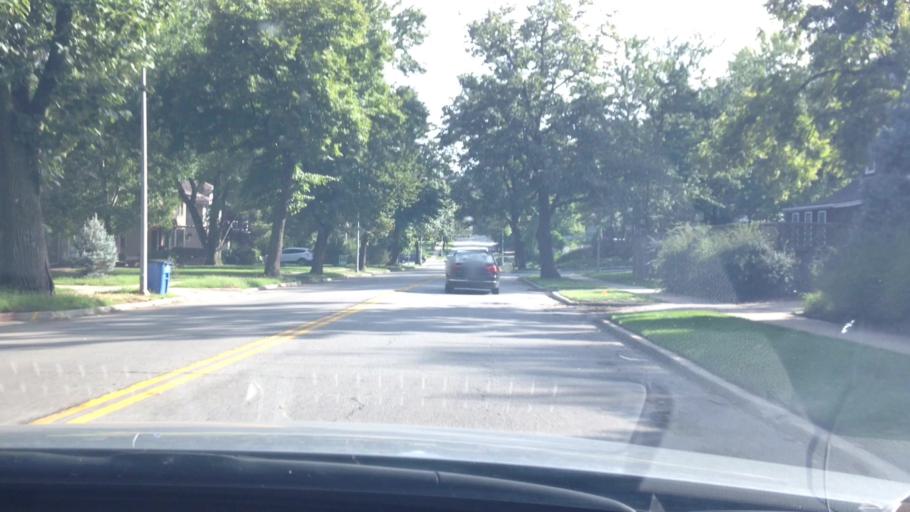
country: US
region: Kansas
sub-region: Johnson County
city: Mission Hills
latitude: 39.0205
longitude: -94.5927
